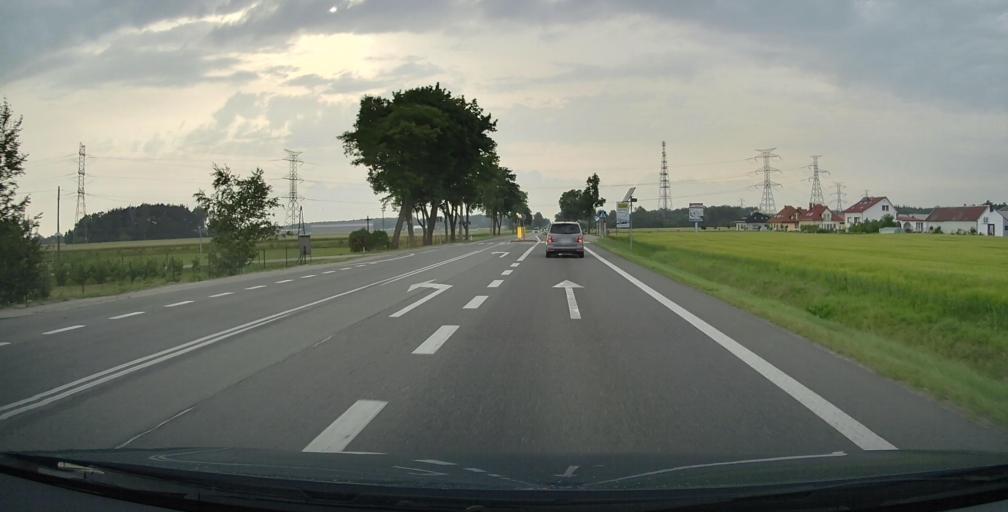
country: PL
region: Masovian Voivodeship
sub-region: Powiat siedlecki
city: Zbuczyn
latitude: 52.1178
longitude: 22.3635
